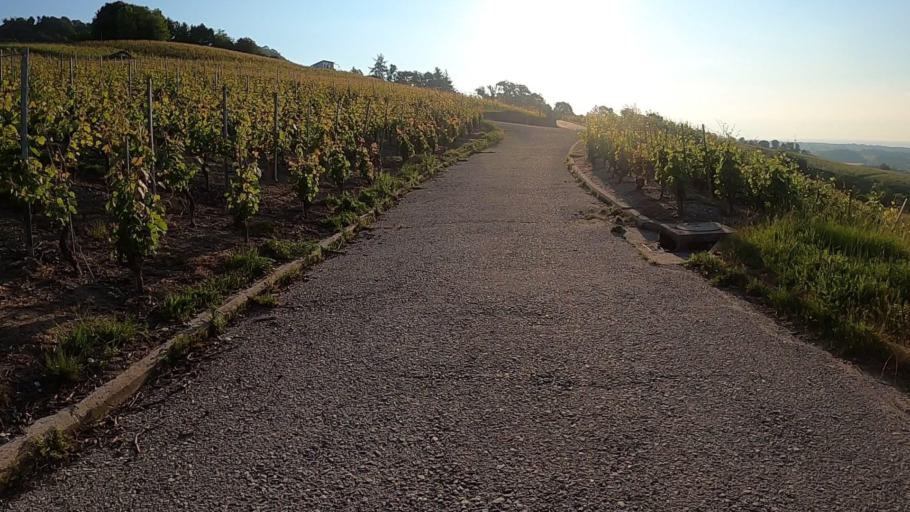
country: CH
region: Vaud
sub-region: Nyon District
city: Rolle
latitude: 46.4752
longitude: 6.3425
